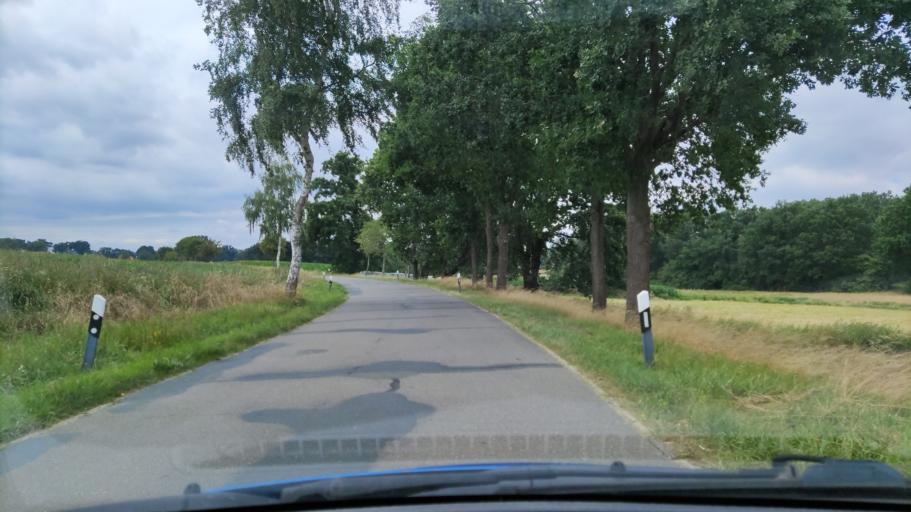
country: DE
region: Lower Saxony
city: Weste
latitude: 53.0795
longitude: 10.6885
